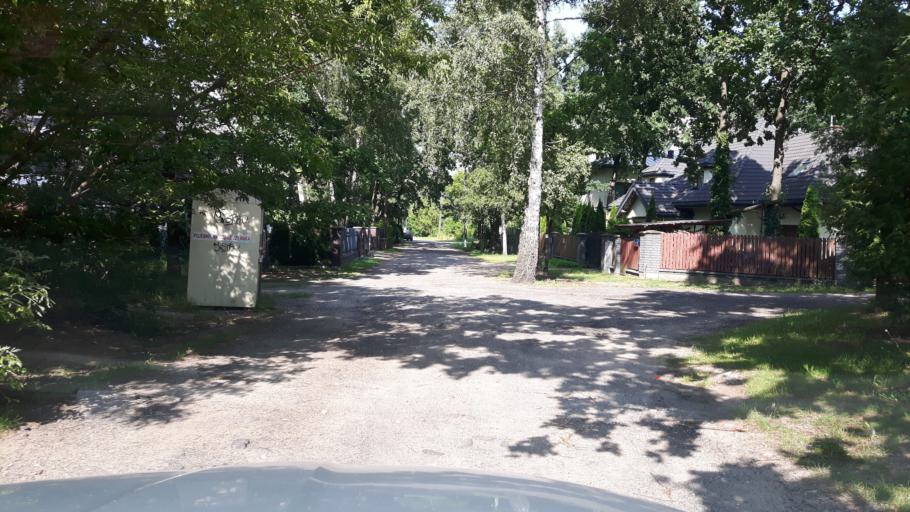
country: PL
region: Masovian Voivodeship
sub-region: Warszawa
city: Rembertow
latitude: 52.2740
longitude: 21.1643
